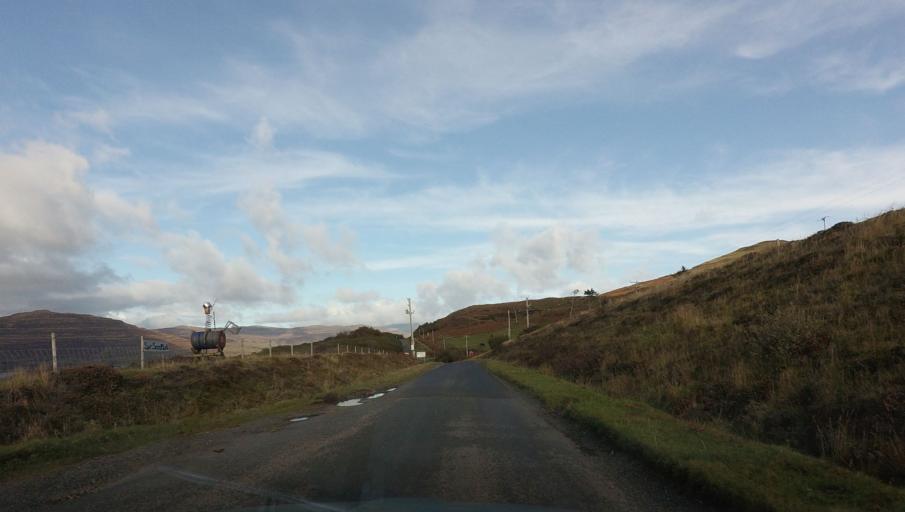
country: GB
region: Scotland
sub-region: Argyll and Bute
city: Isle Of Mull
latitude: 56.3273
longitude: -6.2015
